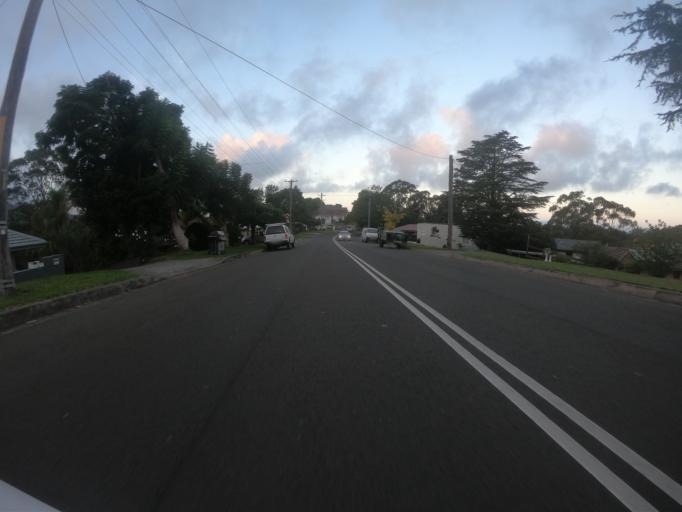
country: AU
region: New South Wales
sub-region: Wollongong
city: Mount Ousley
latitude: -34.3936
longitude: 150.8724
